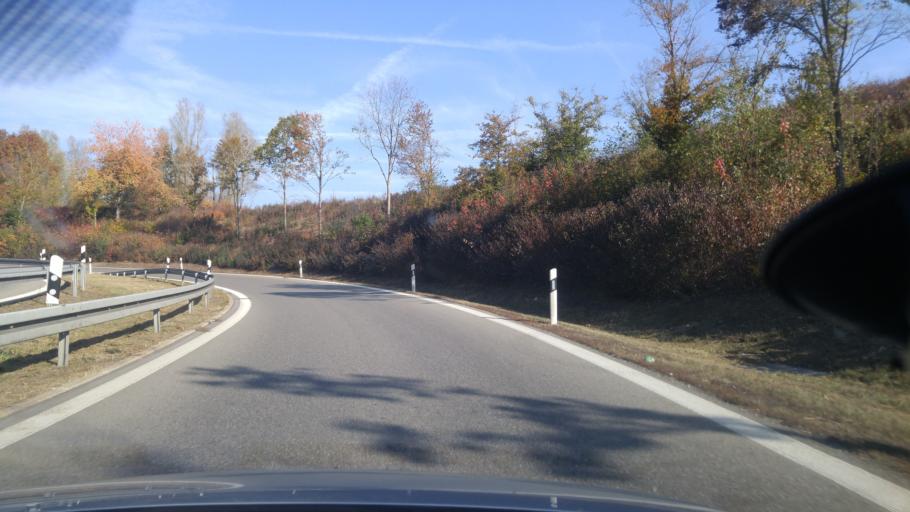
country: DE
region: Baden-Wuerttemberg
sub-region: Karlsruhe Region
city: Empfingen
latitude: 48.3850
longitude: 8.7273
